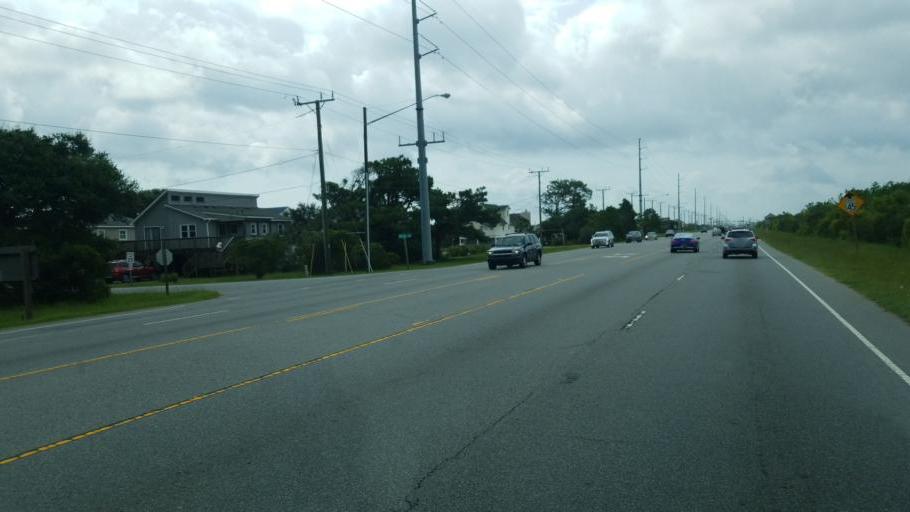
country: US
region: North Carolina
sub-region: Dare County
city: Kill Devil Hills
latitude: 36.0189
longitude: -75.6642
